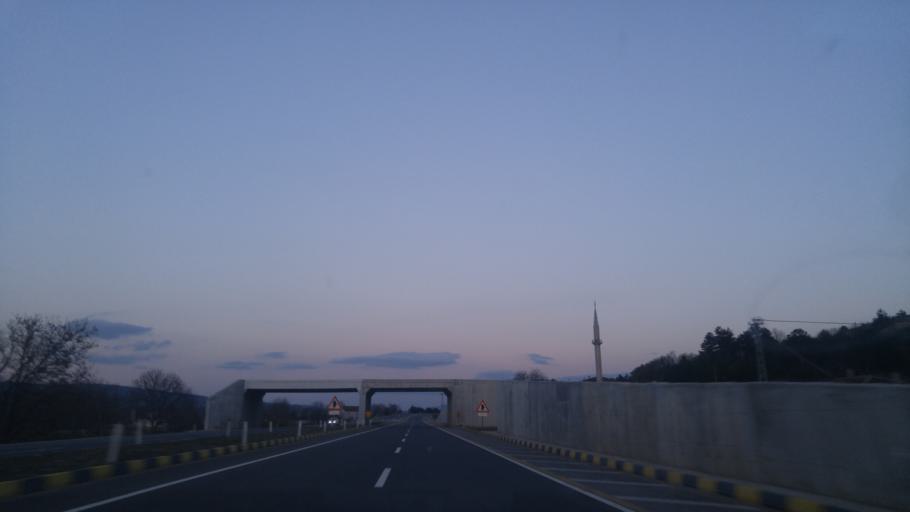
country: TR
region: Kastamonu
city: Igdir
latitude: 41.2287
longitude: 33.0952
